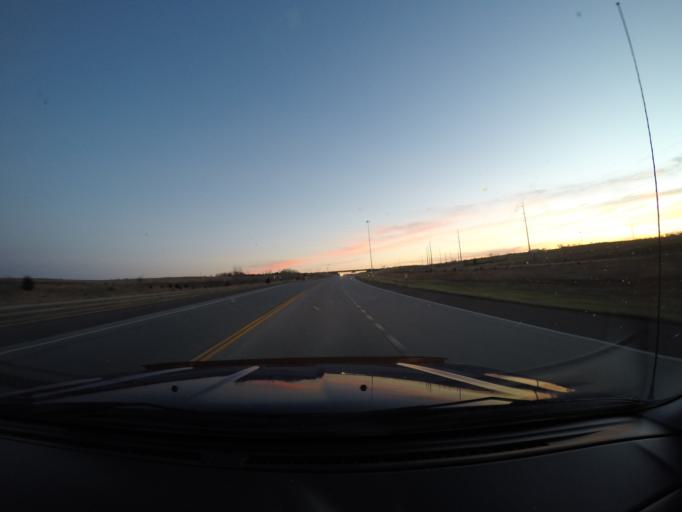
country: US
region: Kansas
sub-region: Douglas County
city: Lawrence
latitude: 38.9781
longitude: -95.3345
